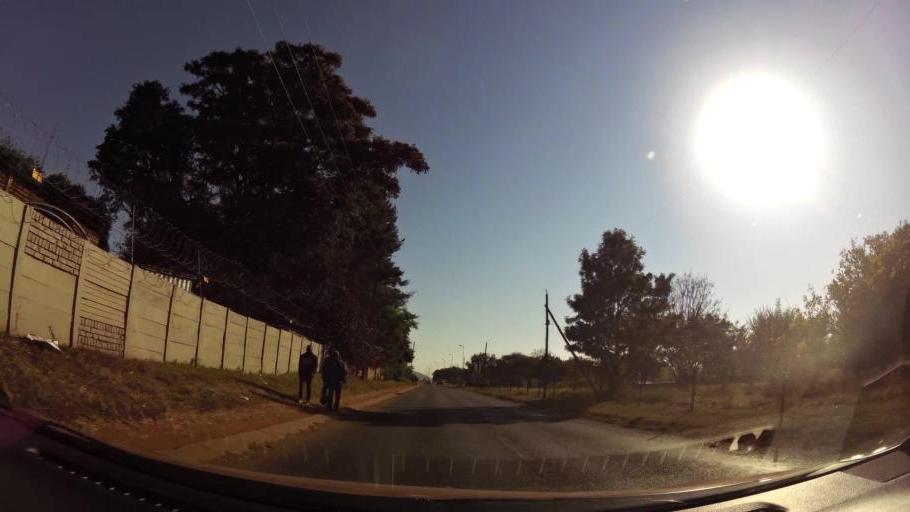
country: ZA
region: Gauteng
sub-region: City of Tshwane Metropolitan Municipality
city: Pretoria
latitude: -25.6589
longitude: 28.1317
